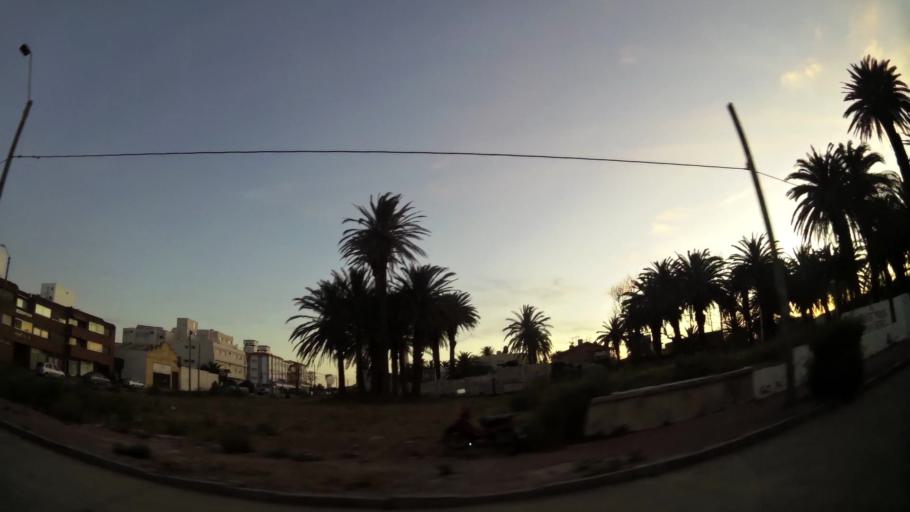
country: UY
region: Maldonado
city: Punta del Este
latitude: -34.9666
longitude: -54.9515
